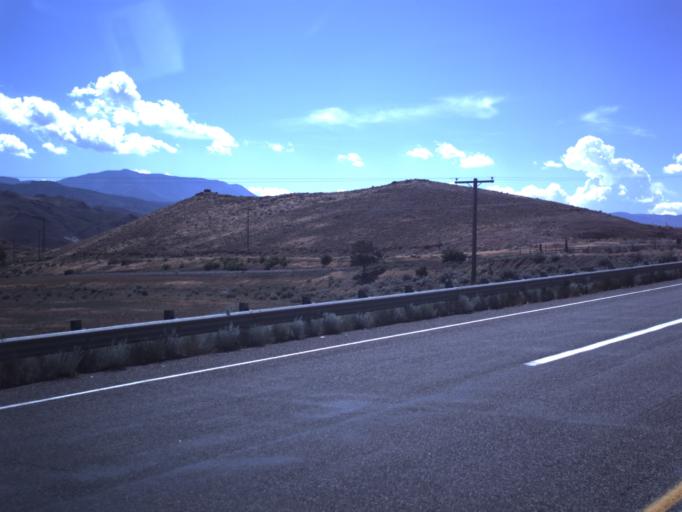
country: US
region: Utah
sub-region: Sevier County
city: Monroe
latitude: 38.4619
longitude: -112.2328
